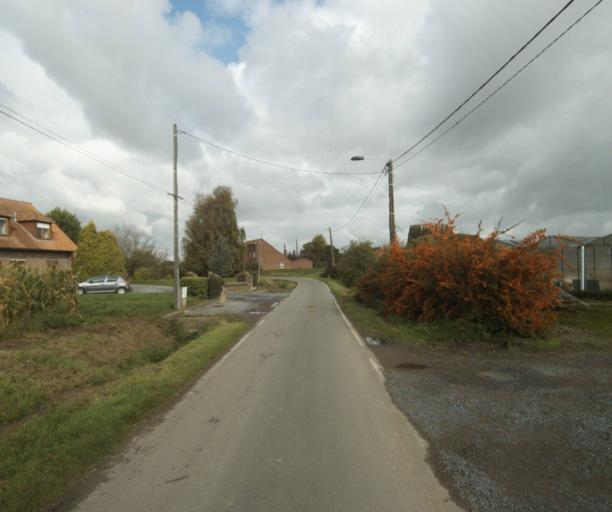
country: FR
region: Nord-Pas-de-Calais
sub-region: Departement du Nord
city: Verlinghem
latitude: 50.6944
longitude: 2.9972
